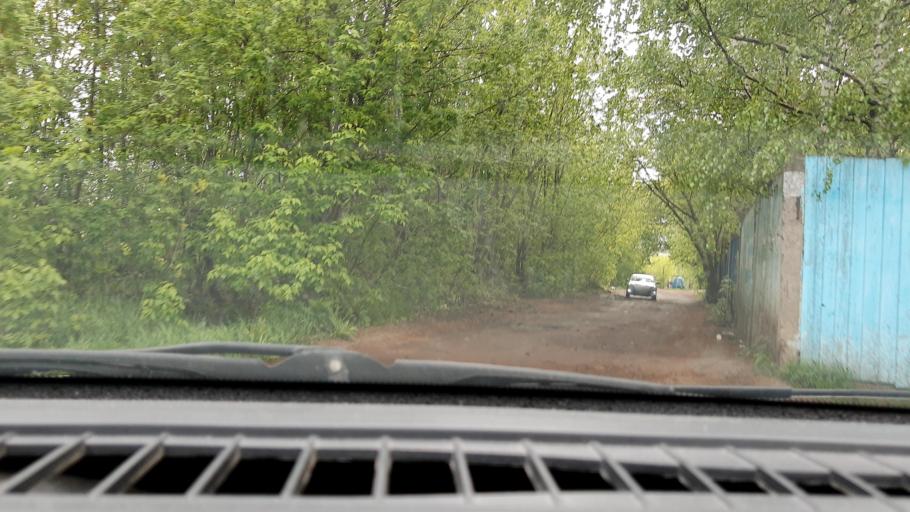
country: RU
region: Nizjnij Novgorod
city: Nizhniy Novgorod
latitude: 56.2708
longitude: 43.8963
